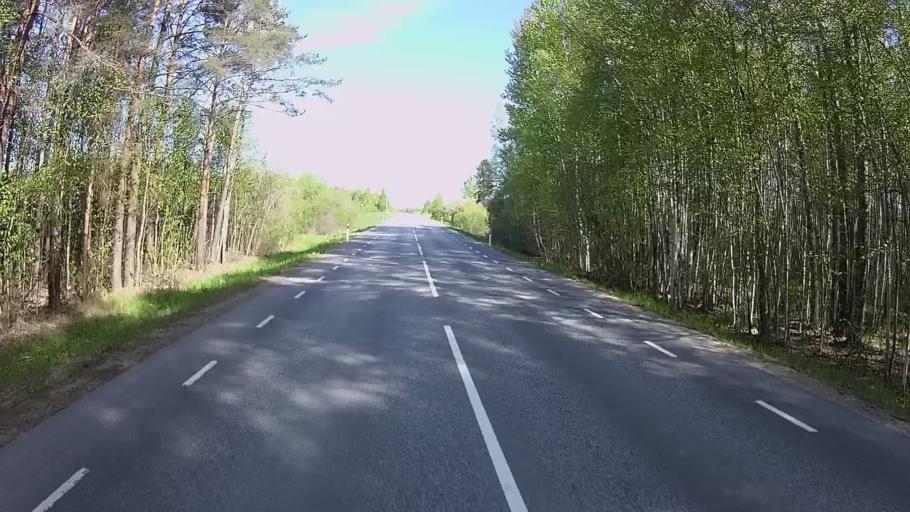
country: EE
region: Polvamaa
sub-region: Raepina vald
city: Rapina
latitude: 58.0617
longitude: 27.5492
